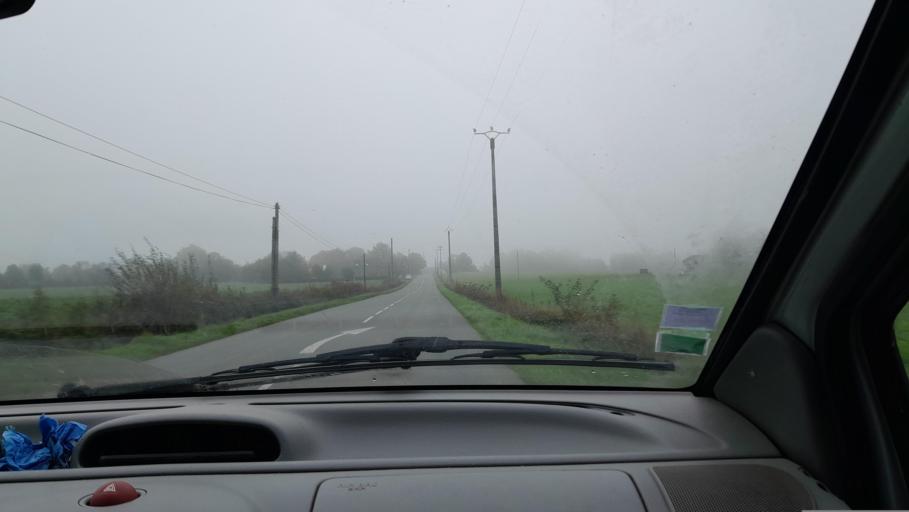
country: FR
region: Pays de la Loire
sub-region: Departement de la Mayenne
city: Ballots
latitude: 47.9611
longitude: -1.0510
